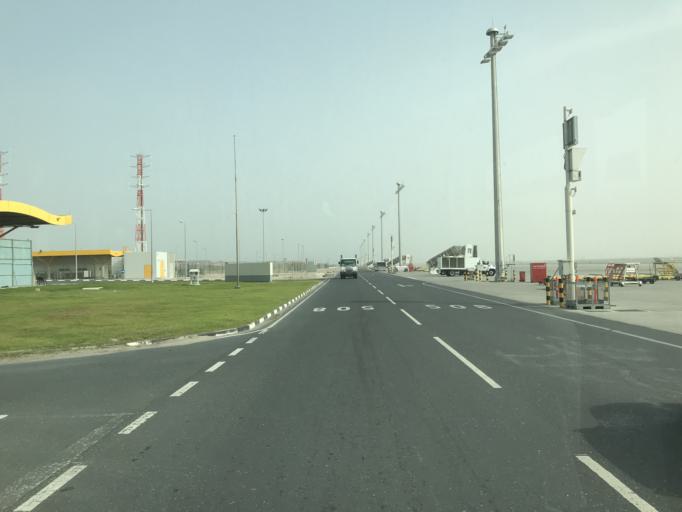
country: QA
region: Baladiyat ad Dawhah
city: Doha
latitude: 25.2773
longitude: 51.5997
